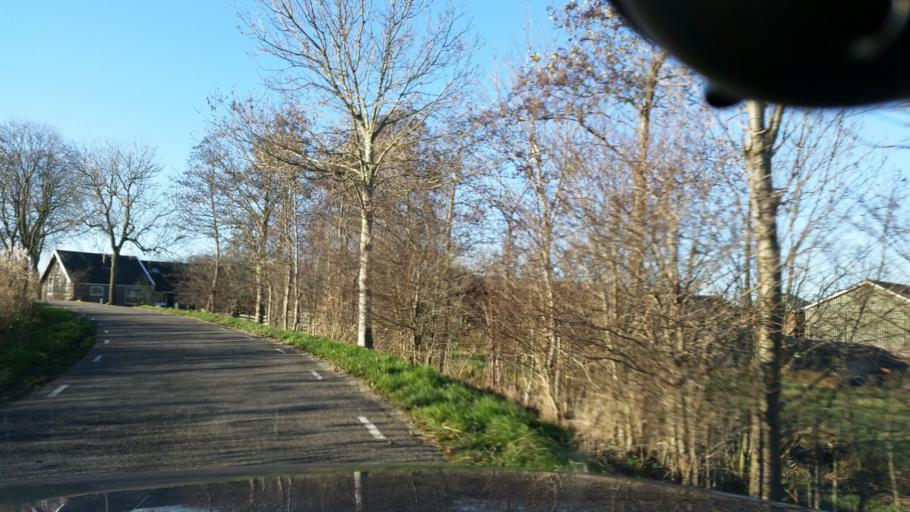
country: NL
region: North Holland
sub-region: Gemeente Ouder-Amstel
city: Ouderkerk aan de Amstel
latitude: 52.2535
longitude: 4.8917
